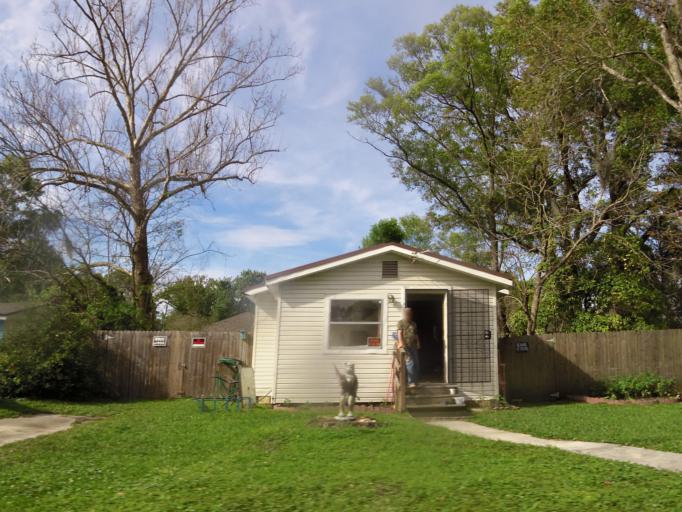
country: US
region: Florida
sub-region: Duval County
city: Jacksonville
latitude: 30.3031
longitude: -81.7418
